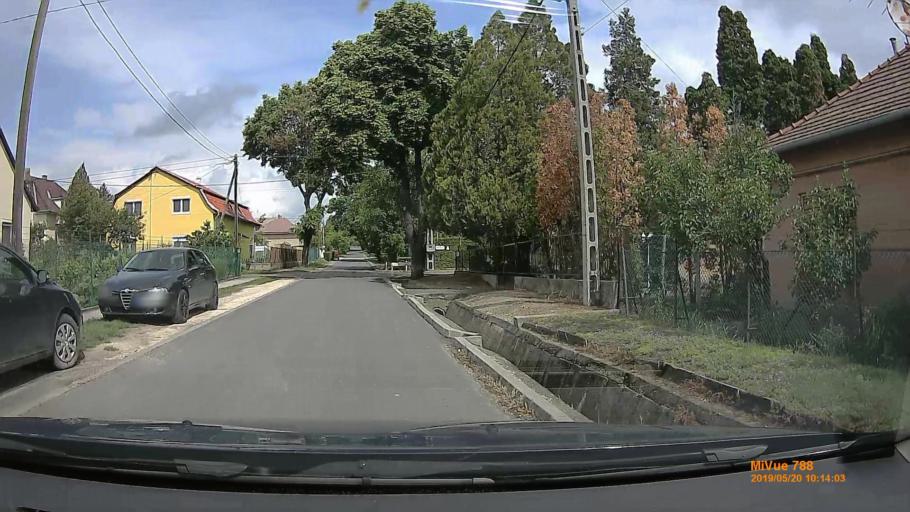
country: HU
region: Budapest
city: Budapest XVII. keruelet
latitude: 47.4897
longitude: 19.2768
